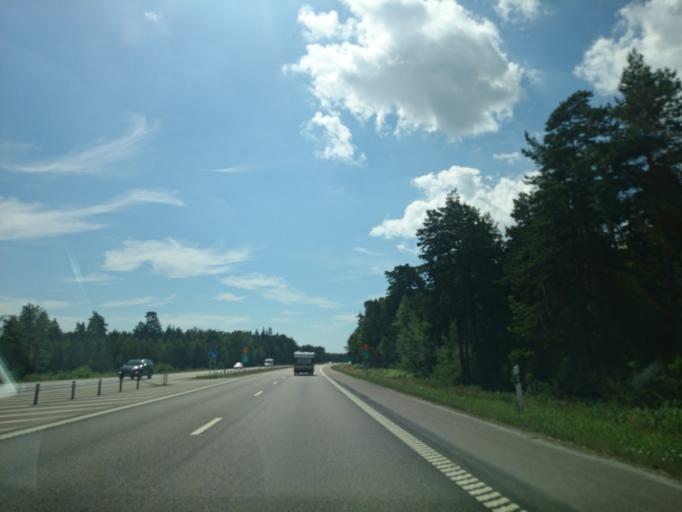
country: SE
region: Kalmar
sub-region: Kalmar Kommun
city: Lindsdal
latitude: 56.7225
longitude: 16.3161
